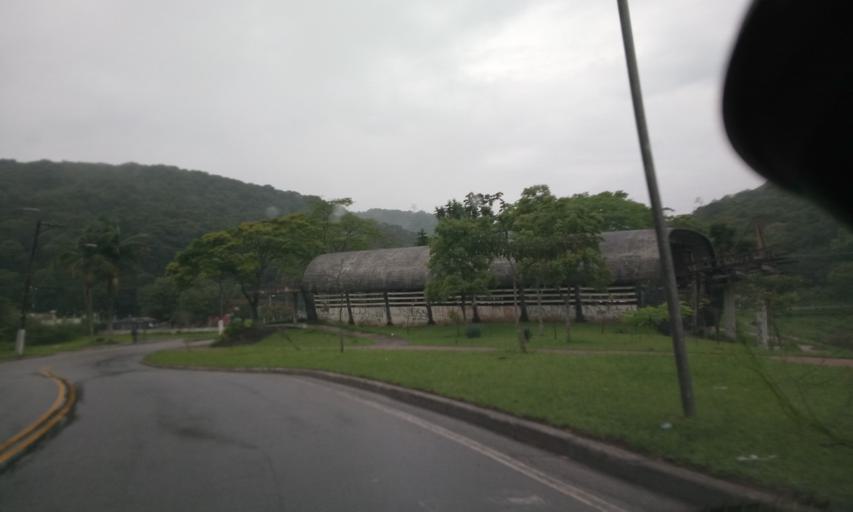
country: BR
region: Sao Paulo
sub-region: Maua
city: Maua
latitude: -23.7293
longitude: -46.4957
